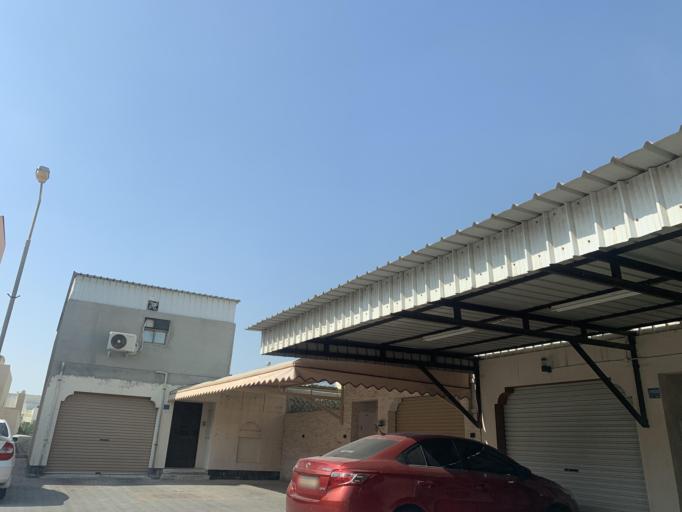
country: BH
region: Central Governorate
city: Madinat Hamad
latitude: 26.1240
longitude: 50.4910
